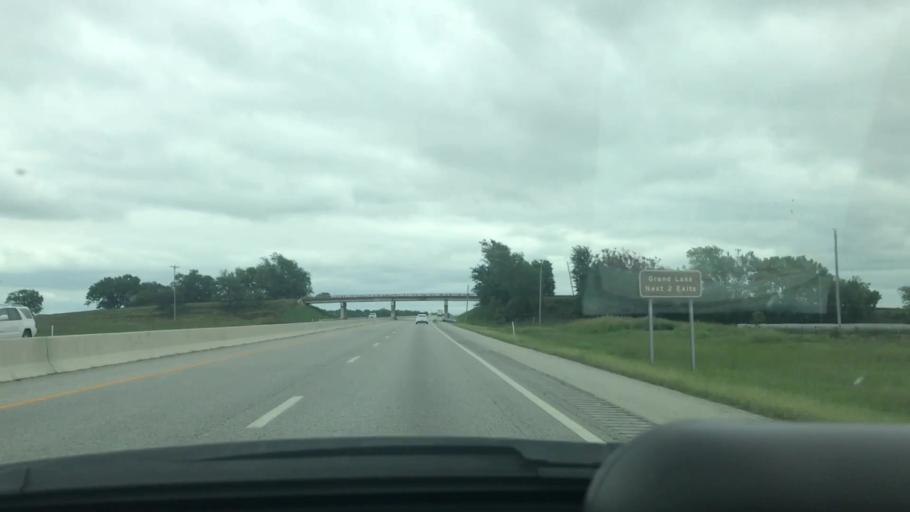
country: US
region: Oklahoma
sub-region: Ottawa County
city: Afton
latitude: 36.7045
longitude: -94.9836
